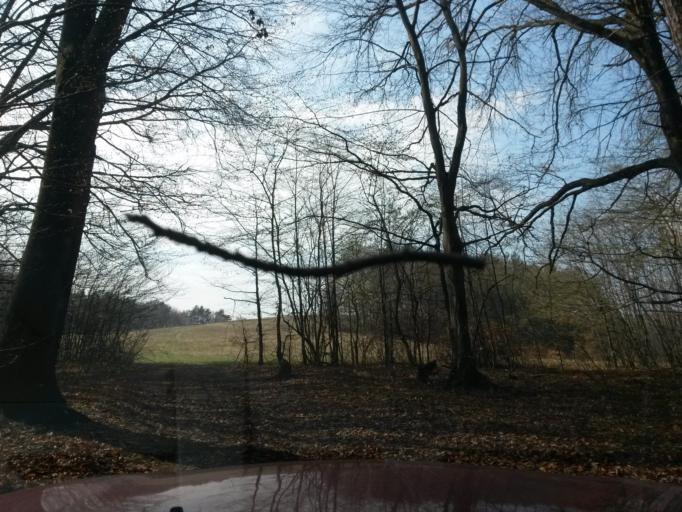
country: SK
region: Presovsky
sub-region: Okres Presov
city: Presov
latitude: 48.9307
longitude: 21.1525
